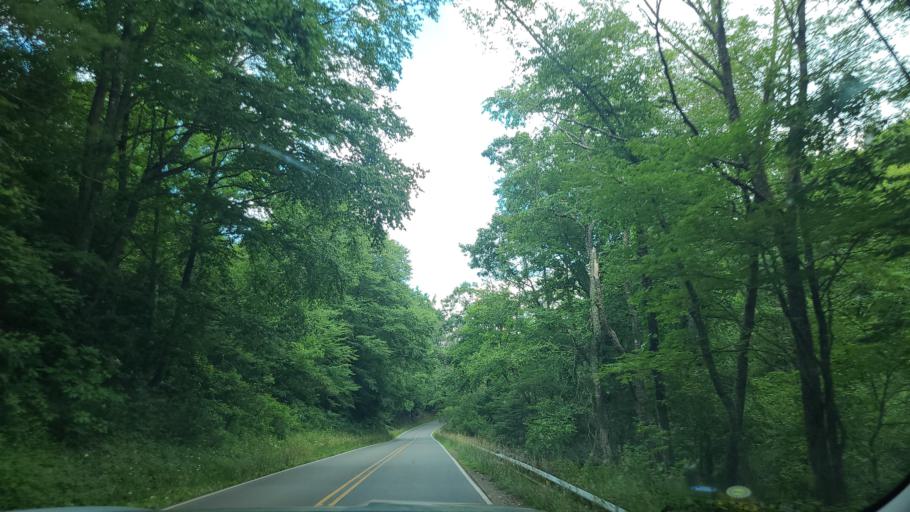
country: US
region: North Carolina
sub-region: Ashe County
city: Jefferson
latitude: 36.3931
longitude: -81.3664
